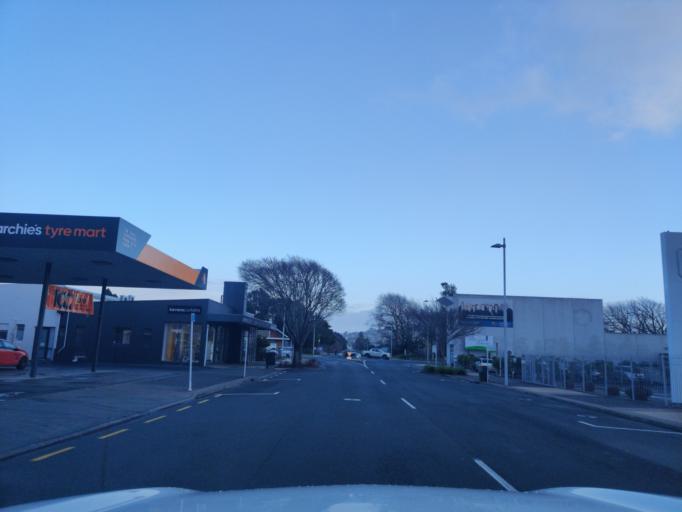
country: NZ
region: Auckland
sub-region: Auckland
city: Pukekohe East
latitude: -37.2010
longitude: 174.9012
